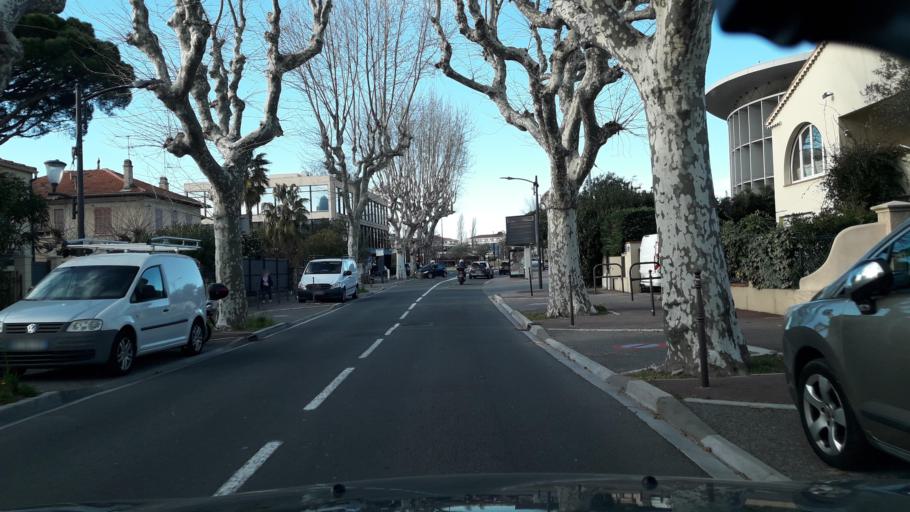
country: FR
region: Provence-Alpes-Cote d'Azur
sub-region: Departement du Var
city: Frejus
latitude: 43.4267
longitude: 6.7375
